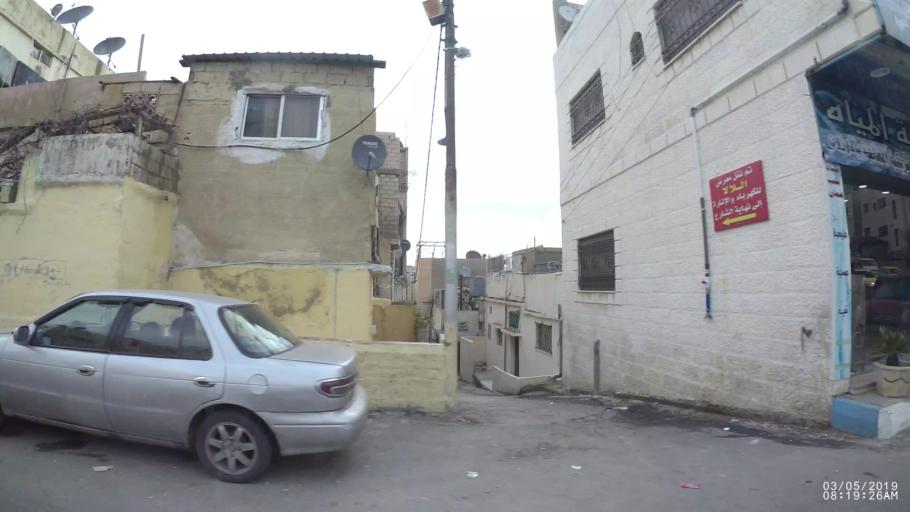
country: JO
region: Amman
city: Amman
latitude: 31.9719
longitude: 35.9221
